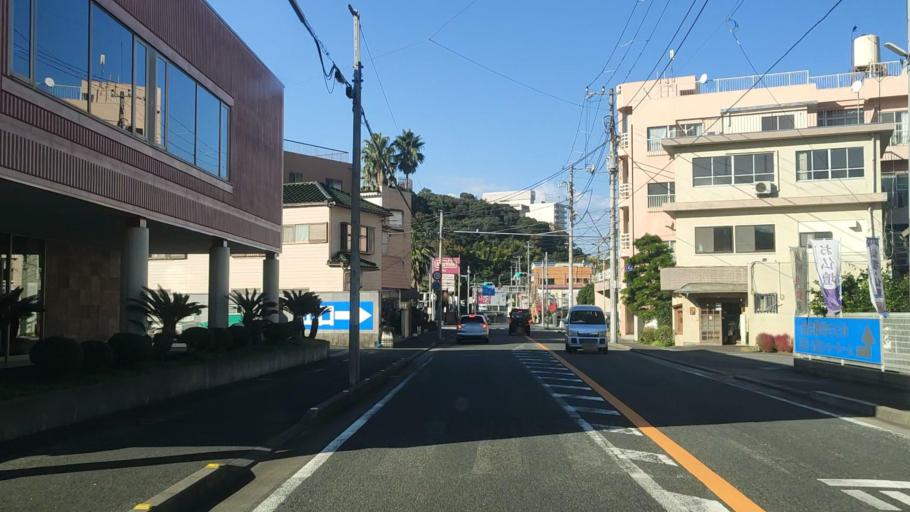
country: JP
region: Shizuoka
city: Ito
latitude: 34.9606
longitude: 139.0915
